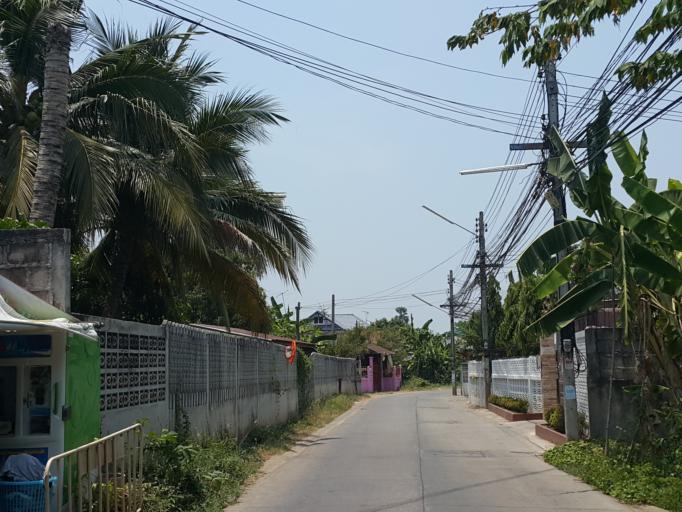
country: TH
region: Phitsanulok
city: Phitsanulok
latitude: 16.8158
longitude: 100.2527
